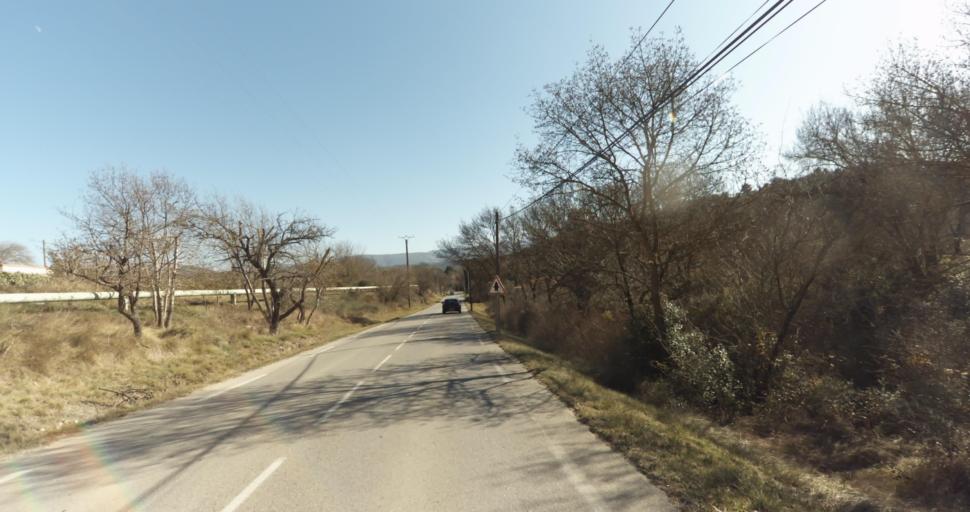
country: FR
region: Provence-Alpes-Cote d'Azur
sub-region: Departement des Bouches-du-Rhone
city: La Bouilladisse
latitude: 43.3949
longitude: 5.5861
